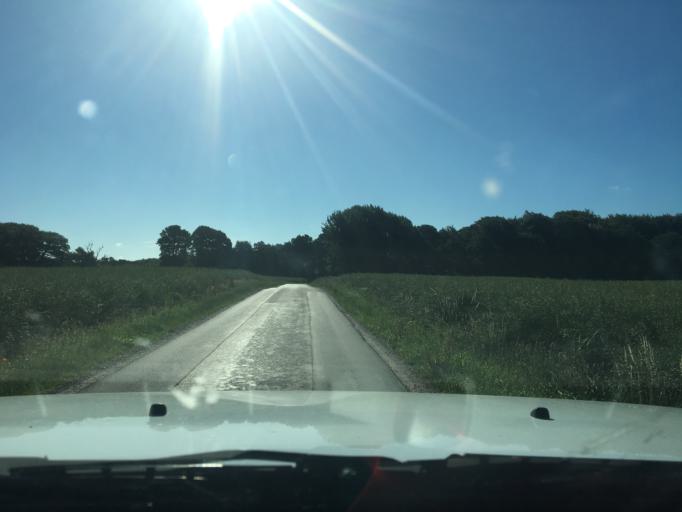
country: DK
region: Central Jutland
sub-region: Syddjurs Kommune
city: Hornslet
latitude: 56.3130
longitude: 10.2715
